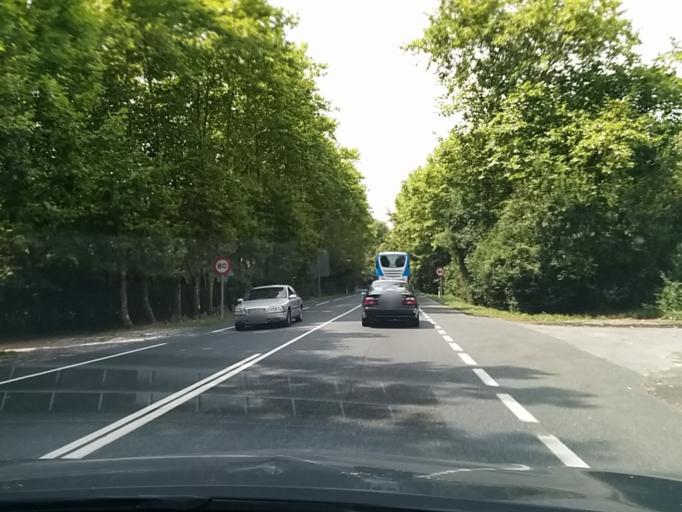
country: ES
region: Basque Country
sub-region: Provincia de Guipuzcoa
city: Irun
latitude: 43.3423
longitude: -1.8191
